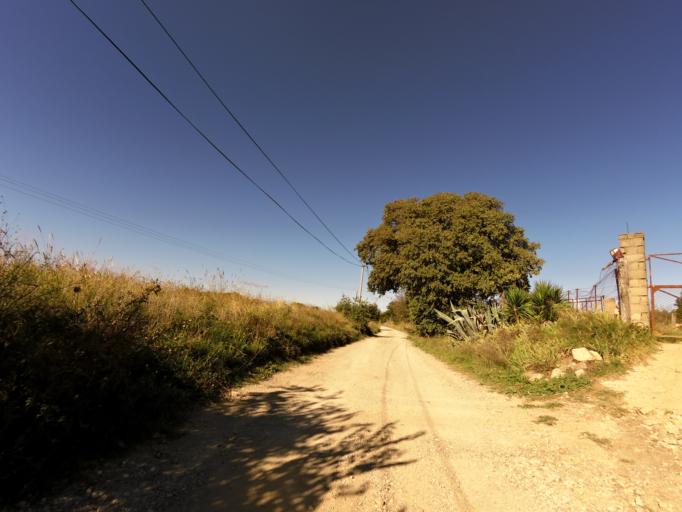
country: FR
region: Languedoc-Roussillon
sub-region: Departement du Gard
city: Gallargues-le-Montueux
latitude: 43.7256
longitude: 4.1553
